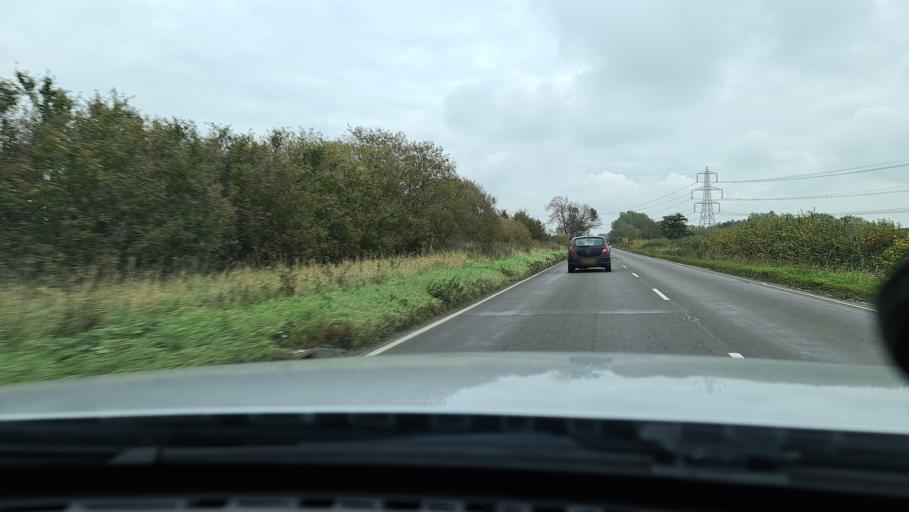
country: GB
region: England
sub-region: Buckinghamshire
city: Steeple Claydon
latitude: 51.8715
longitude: -1.0346
